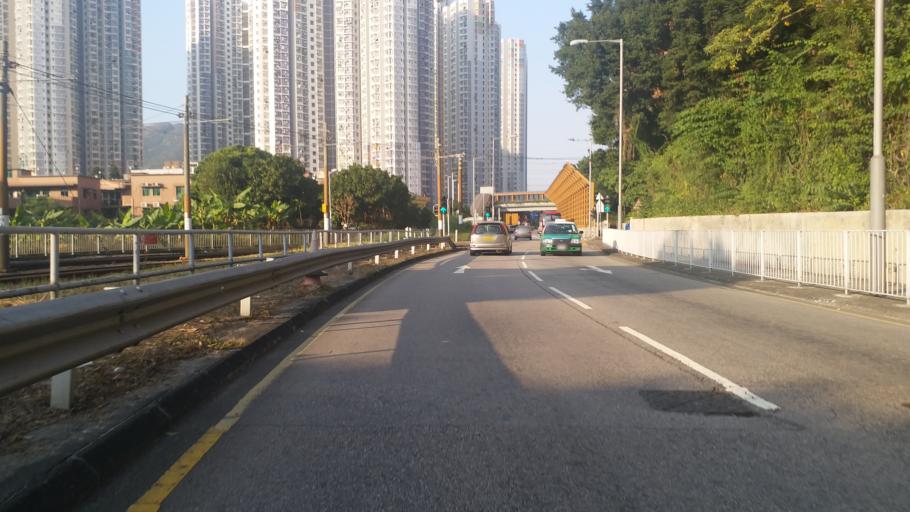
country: HK
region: Tuen Mun
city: Tuen Mun
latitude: 22.4119
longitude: 113.9764
